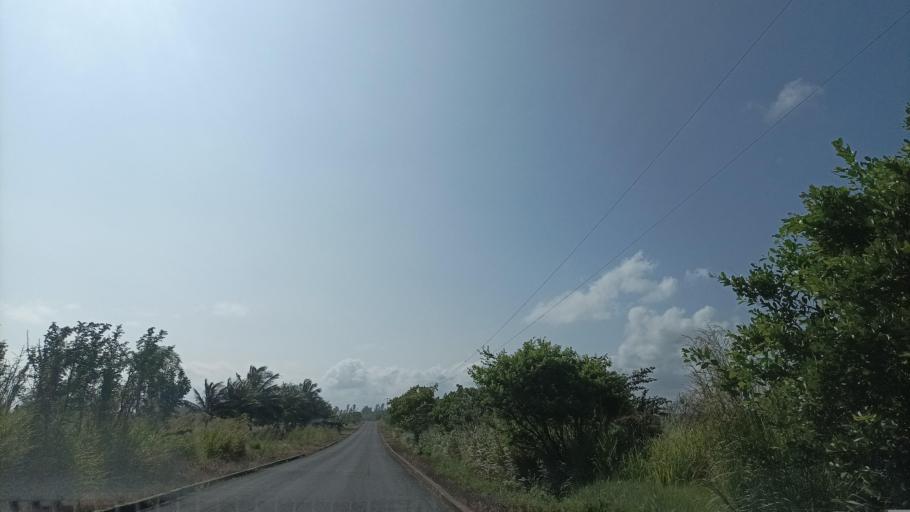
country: MX
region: Veracruz
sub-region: Pajapan
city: Pajapan
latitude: 18.2262
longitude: -94.6178
